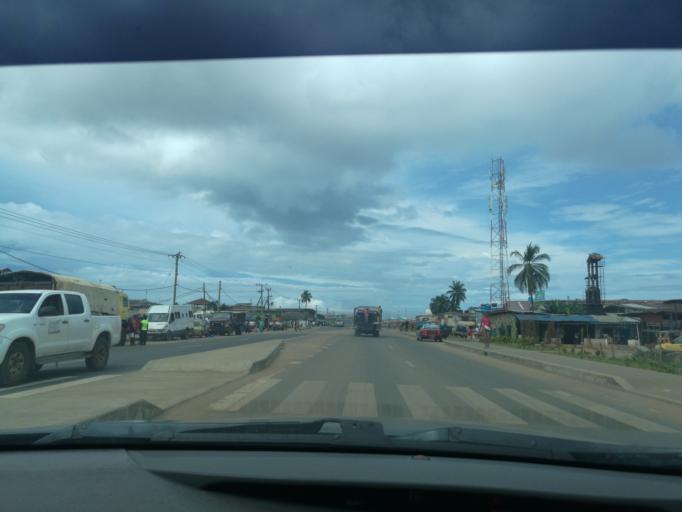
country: LR
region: Montserrado
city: Monrovia
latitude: 6.3385
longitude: -10.7887
